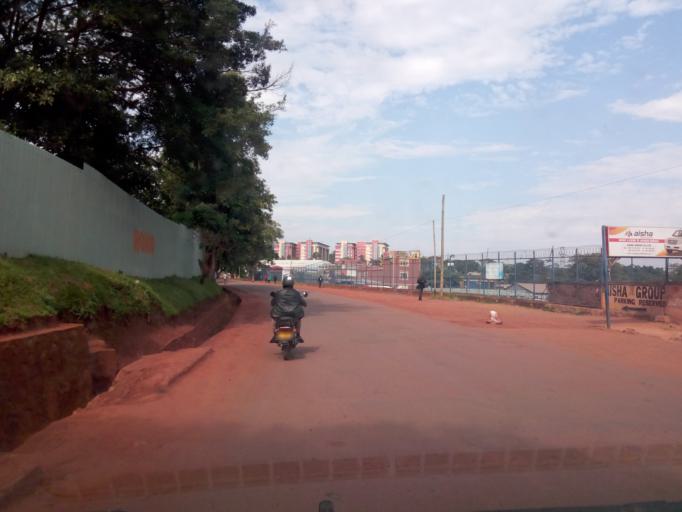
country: UG
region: Central Region
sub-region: Kampala District
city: Kampala
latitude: 0.3292
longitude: 32.6074
